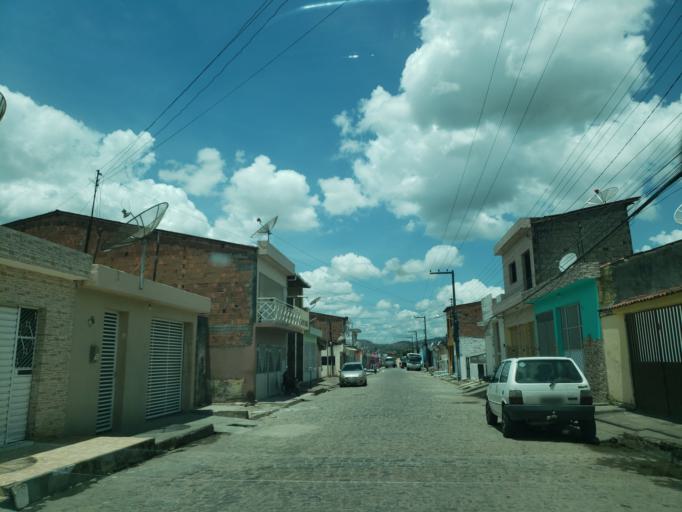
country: BR
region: Alagoas
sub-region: Uniao Dos Palmares
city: Uniao dos Palmares
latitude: -9.1647
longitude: -36.0234
